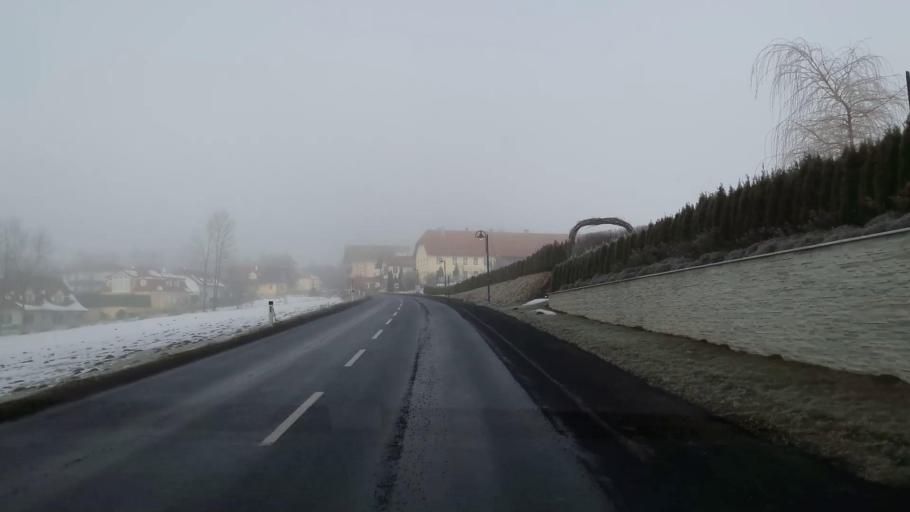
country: AT
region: Lower Austria
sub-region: Politischer Bezirk Neunkirchen
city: Sankt Corona am Wechsel
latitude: 47.5757
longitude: 16.0275
